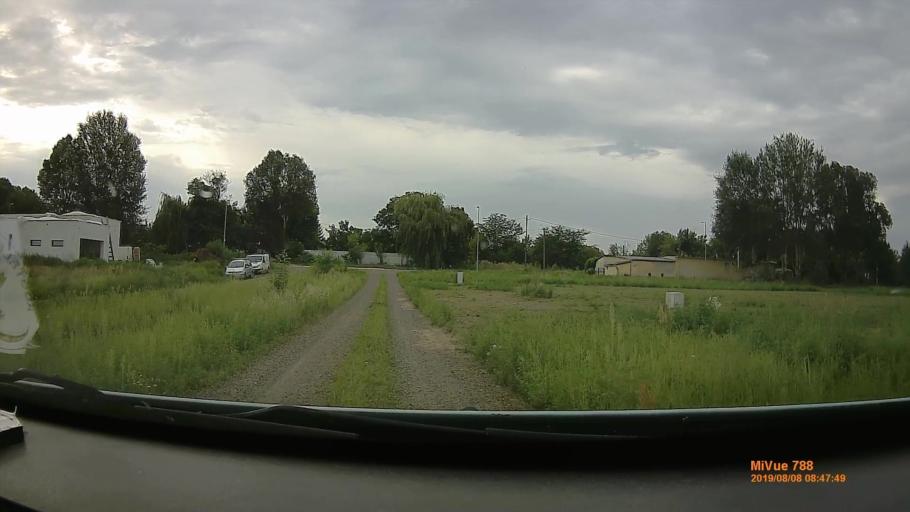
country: HU
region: Hajdu-Bihar
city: Debrecen
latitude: 47.5973
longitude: 21.6380
